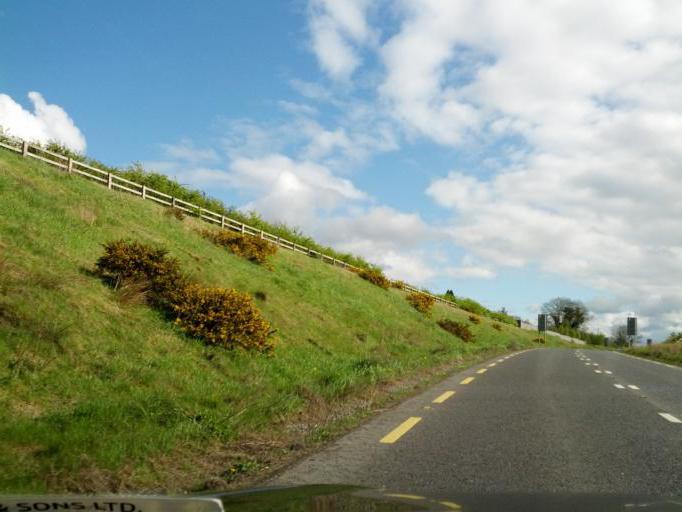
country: IE
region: Leinster
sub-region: Kildare
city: Kilcock
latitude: 53.4776
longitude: -6.7185
